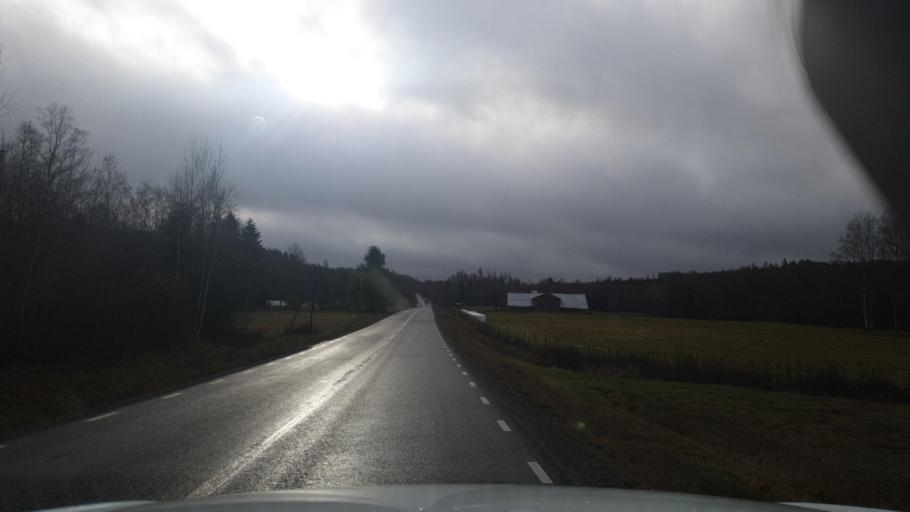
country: SE
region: Vaermland
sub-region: Arjangs Kommun
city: Arjaeng
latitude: 59.5821
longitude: 12.1235
